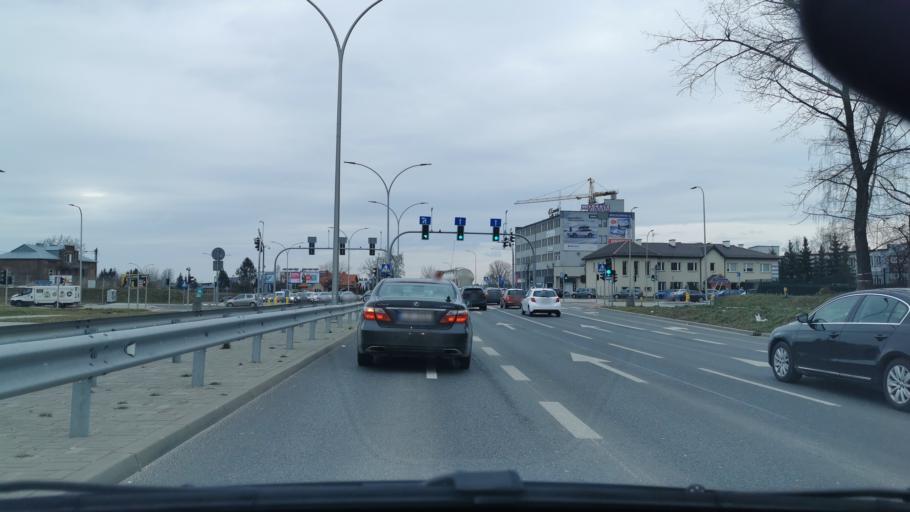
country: PL
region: Lublin Voivodeship
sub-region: Powiat lubelski
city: Lublin
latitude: 51.2465
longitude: 22.5069
